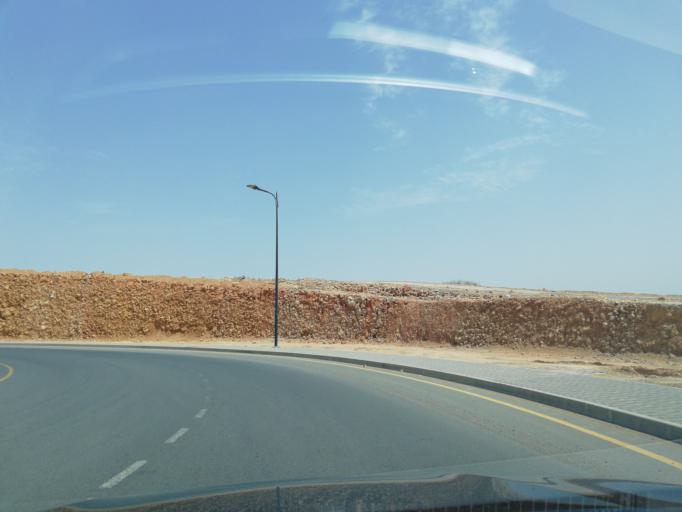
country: OM
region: Muhafazat Masqat
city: Bawshar
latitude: 23.5776
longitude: 58.3279
